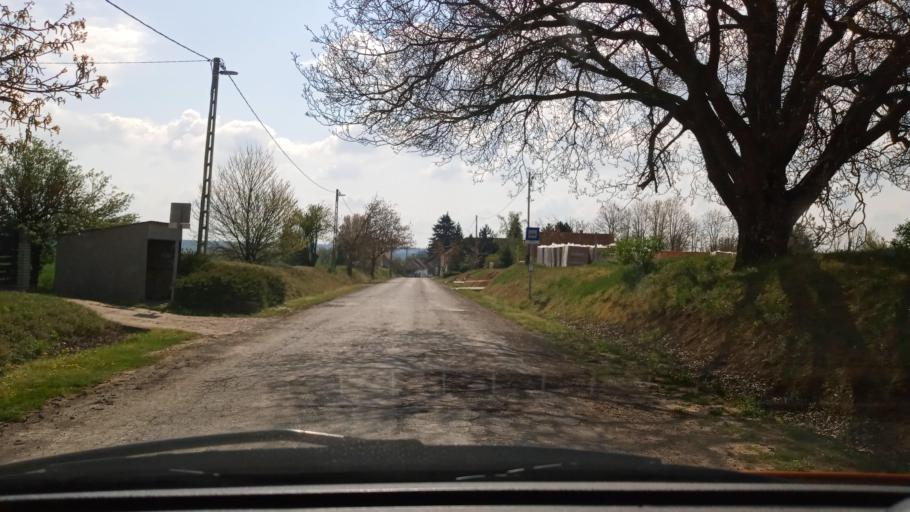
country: HU
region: Baranya
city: Boly
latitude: 46.0820
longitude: 18.5093
